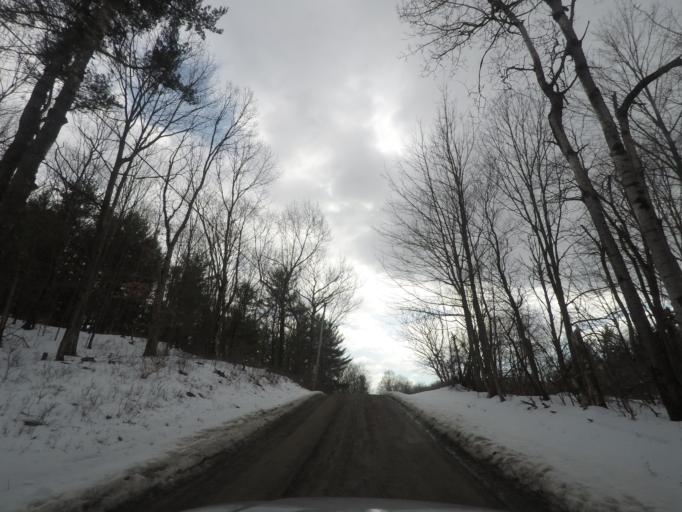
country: US
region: New York
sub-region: Saratoga County
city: Waterford
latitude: 42.7857
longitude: -73.6099
